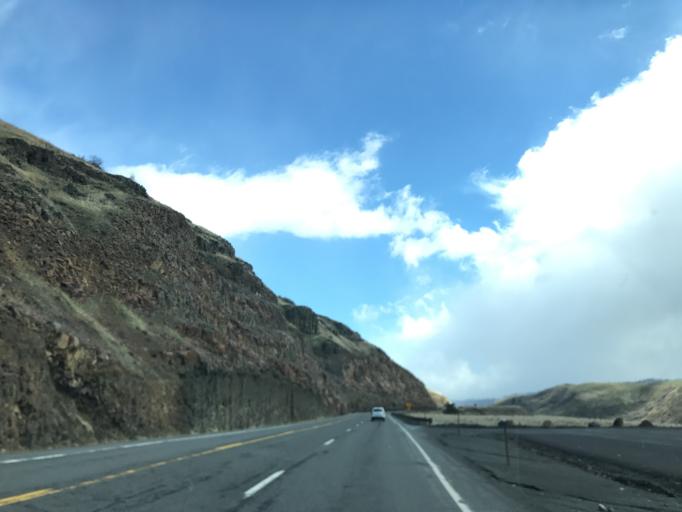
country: US
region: Idaho
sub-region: Idaho County
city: Grangeville
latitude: 45.8187
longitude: -116.2734
